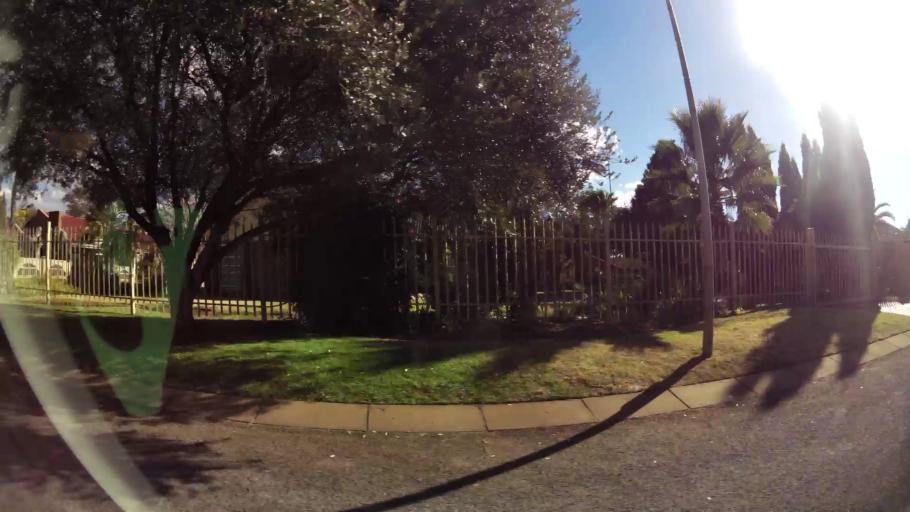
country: ZA
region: North-West
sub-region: Dr Kenneth Kaunda District Municipality
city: Klerksdorp
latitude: -26.8193
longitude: 26.6657
